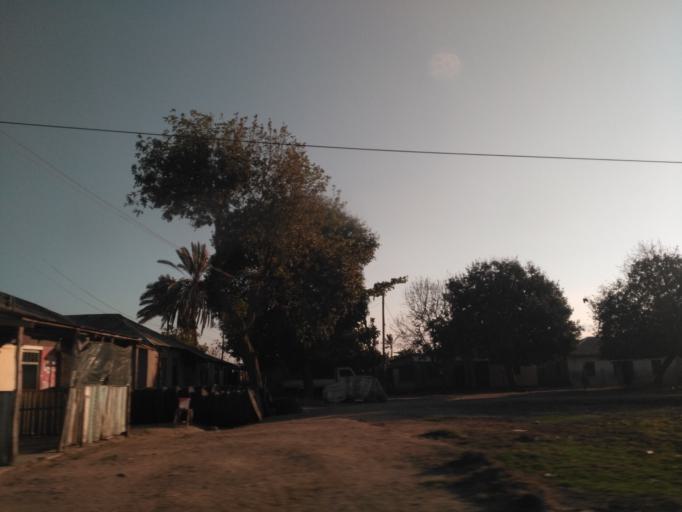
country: TZ
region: Dodoma
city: Dodoma
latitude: -6.1731
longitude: 35.7388
